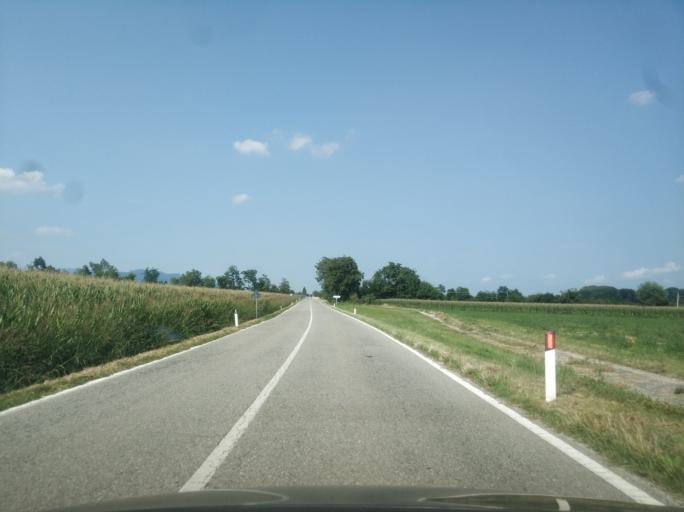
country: IT
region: Piedmont
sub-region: Provincia di Cuneo
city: Caraglio
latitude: 44.4424
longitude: 7.4532
